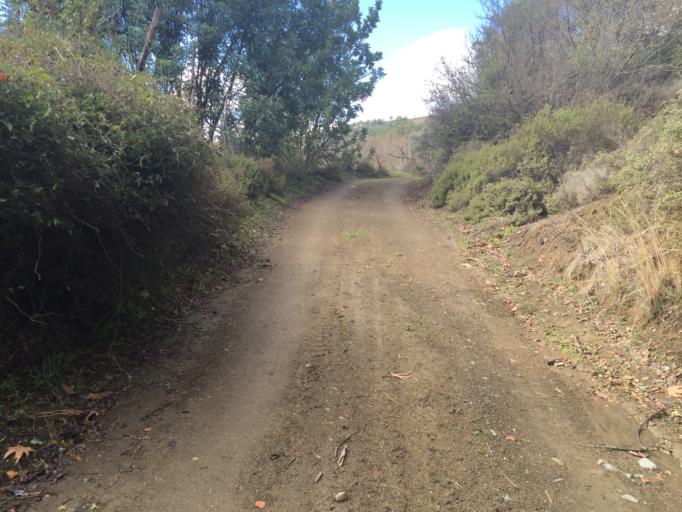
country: CY
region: Limassol
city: Pachna
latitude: 34.8889
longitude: 32.6825
